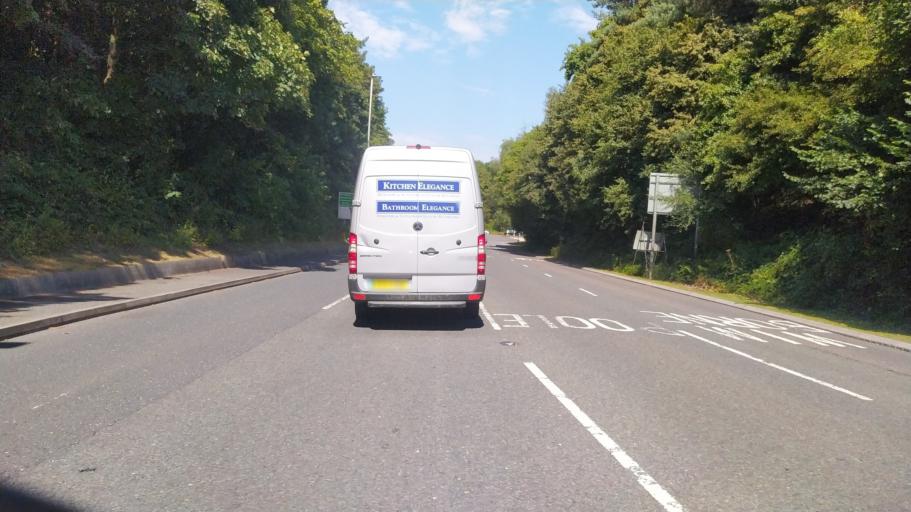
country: GB
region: England
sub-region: Dorset
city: Wimborne Minster
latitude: 50.7858
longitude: -1.9782
